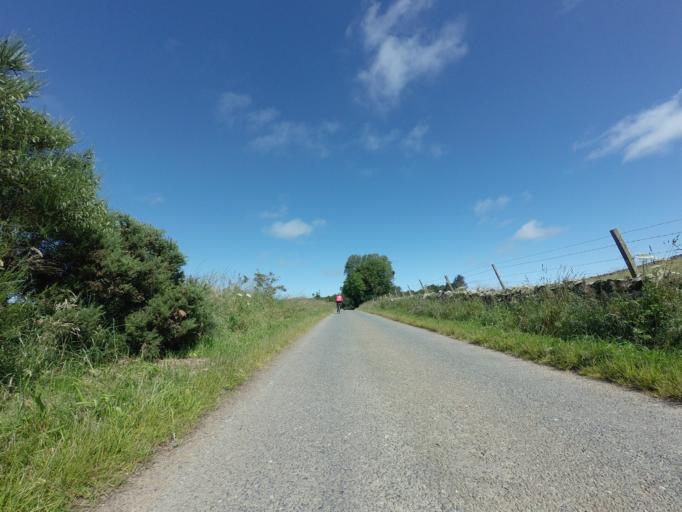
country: GB
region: Scotland
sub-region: Aberdeenshire
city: Banff
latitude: 57.6040
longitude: -2.5128
